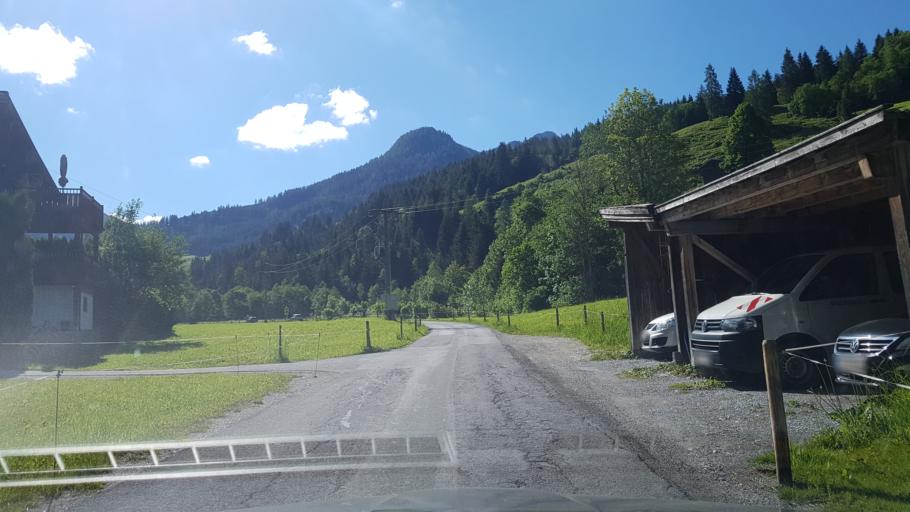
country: AT
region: Salzburg
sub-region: Politischer Bezirk Sankt Johann im Pongau
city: Huttschlag
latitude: 47.2358
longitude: 13.2359
